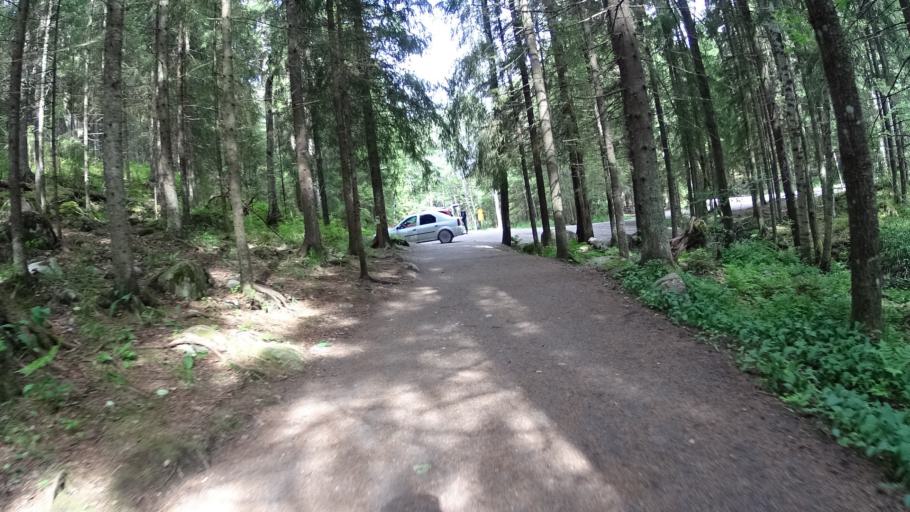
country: FI
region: Uusimaa
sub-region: Helsinki
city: Espoo
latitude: 60.3094
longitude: 24.5179
